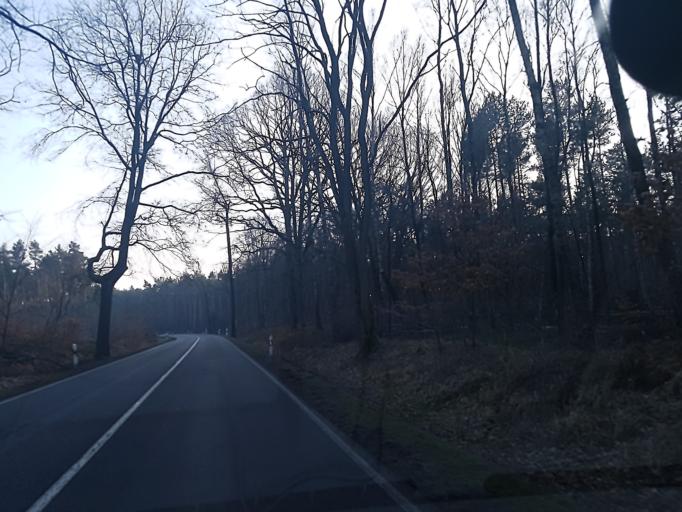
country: DE
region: Brandenburg
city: Wiesenburg
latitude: 52.0170
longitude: 12.4602
